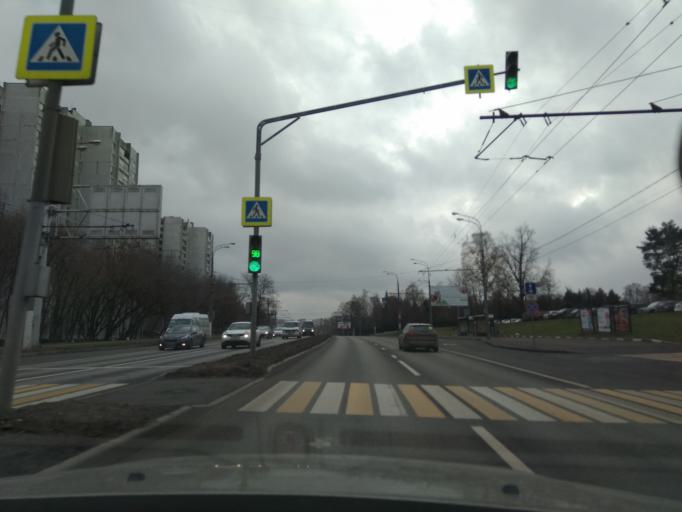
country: RU
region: Moscow
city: Tsaritsyno
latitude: 55.6200
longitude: 37.6570
